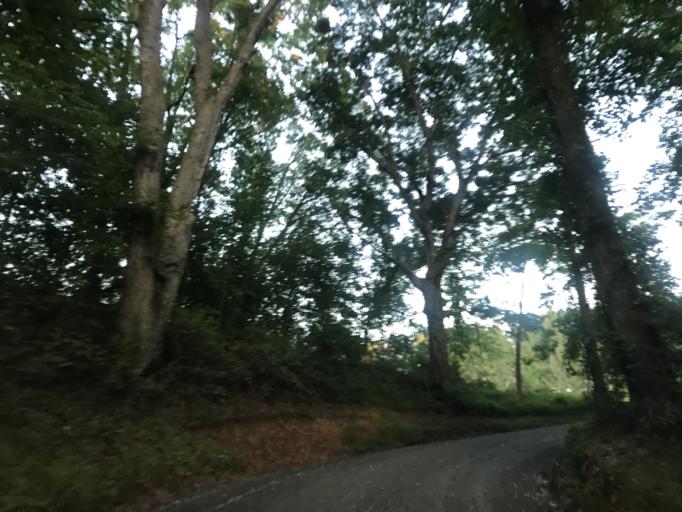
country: US
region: Maryland
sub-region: Harford County
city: Jarrettsville
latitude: 39.6709
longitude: -76.5336
